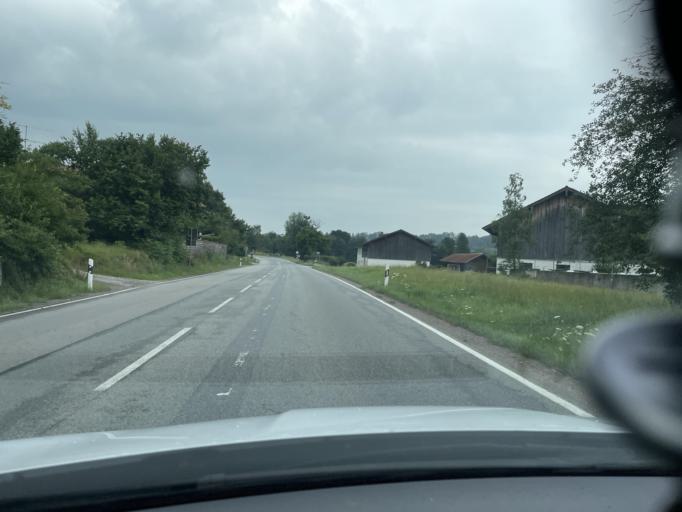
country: DE
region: Bavaria
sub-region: Upper Bavaria
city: Griesstatt
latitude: 47.9791
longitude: 12.1411
